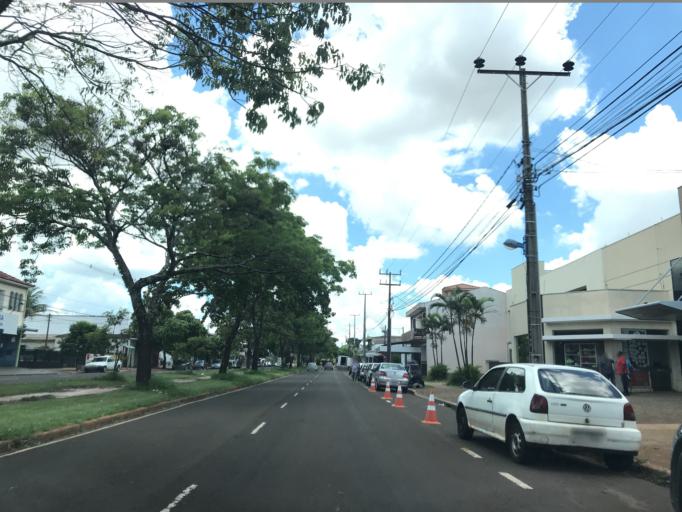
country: BR
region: Parana
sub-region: Maringa
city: Maringa
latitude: -23.3920
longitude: -51.9168
